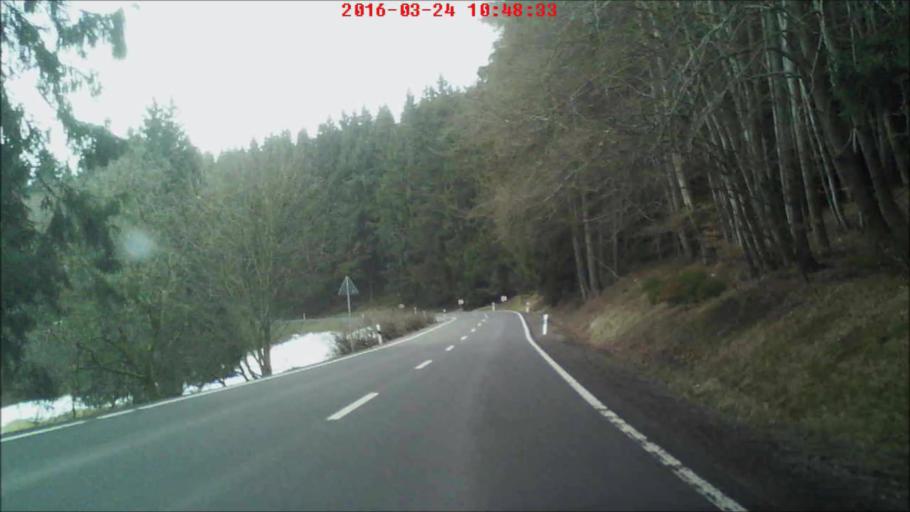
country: DE
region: Thuringia
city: Mohrenbach
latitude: 50.6048
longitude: 10.9842
